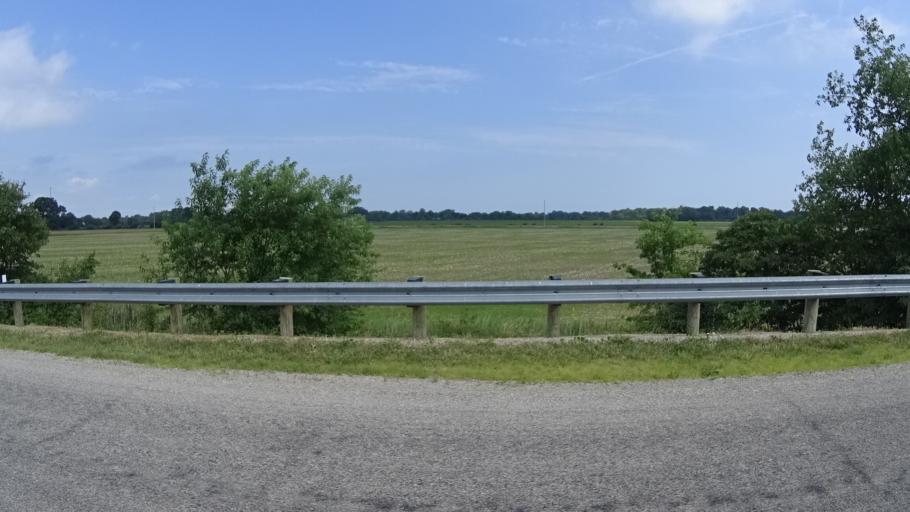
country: US
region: Ohio
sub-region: Lorain County
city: Vermilion
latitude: 41.3836
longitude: -82.4191
